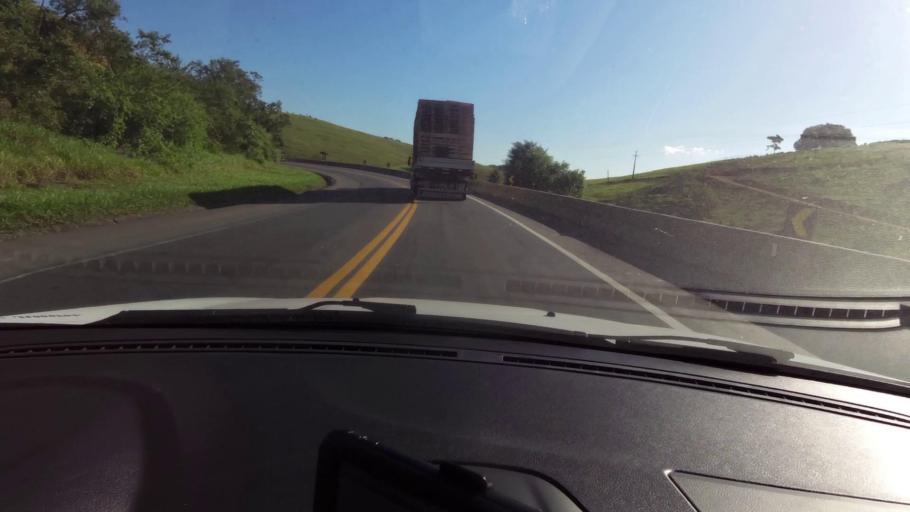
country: BR
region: Espirito Santo
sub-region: Alfredo Chaves
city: Alfredo Chaves
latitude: -20.6667
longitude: -40.6621
